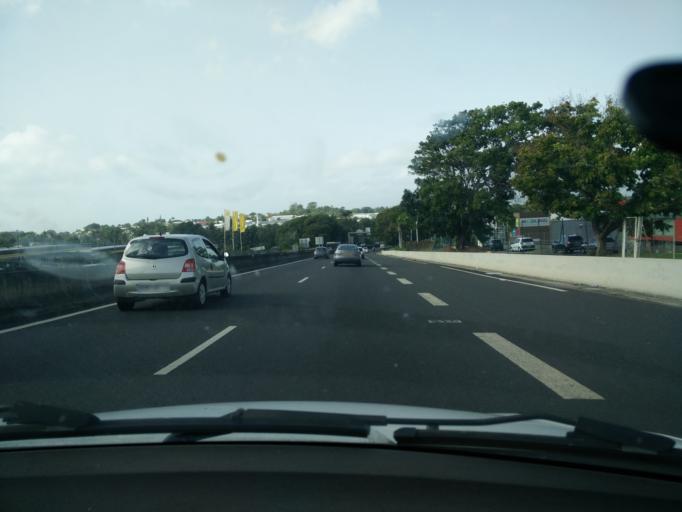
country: GP
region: Guadeloupe
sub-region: Guadeloupe
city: Baie-Mahault
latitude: 16.2381
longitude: -61.5889
